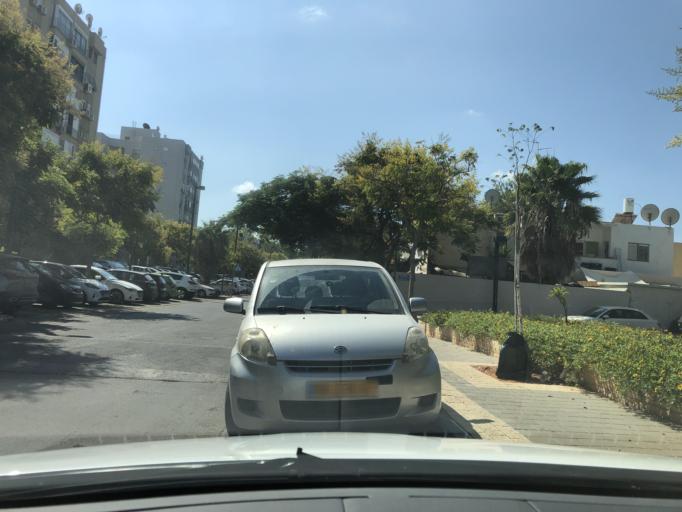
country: IL
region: Tel Aviv
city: Yafo
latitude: 32.0433
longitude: 34.7567
